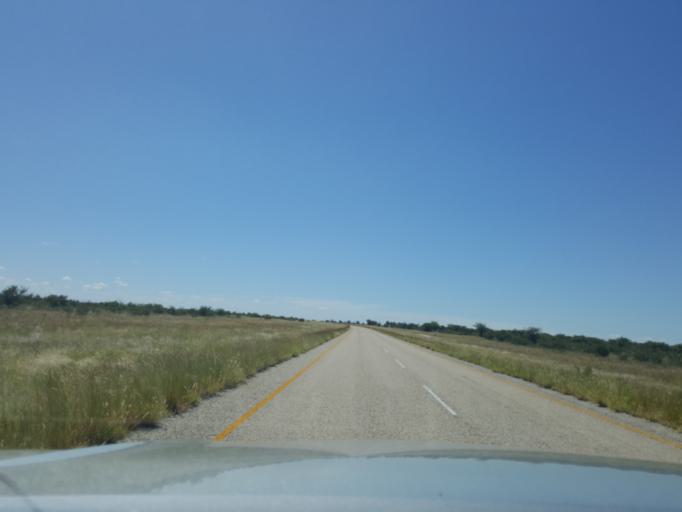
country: BW
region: Central
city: Gweta
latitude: -20.2208
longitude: 25.0506
